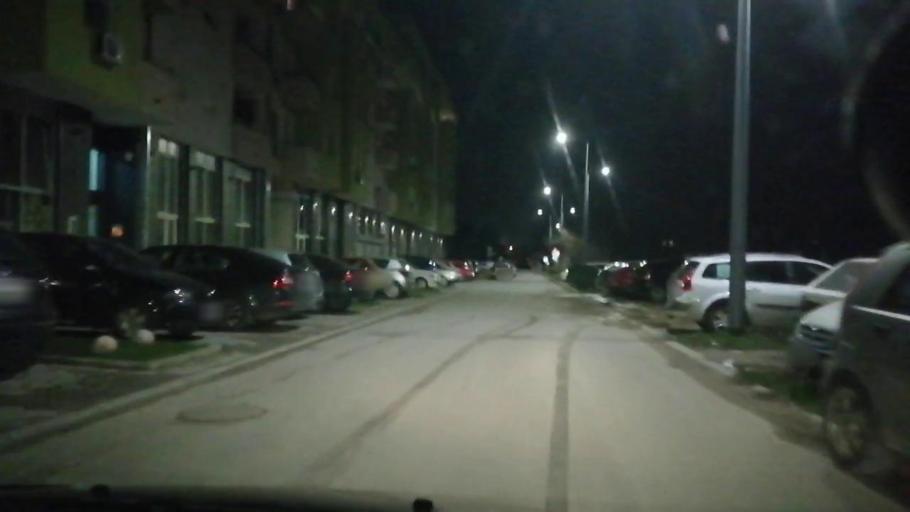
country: RS
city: Veternik
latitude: 45.2424
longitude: 19.7940
